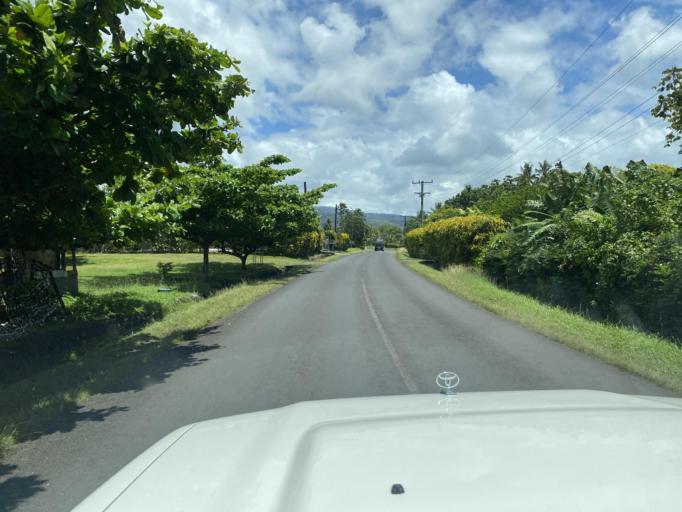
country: WS
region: Tuamasaga
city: Apia
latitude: -13.8429
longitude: -171.7752
